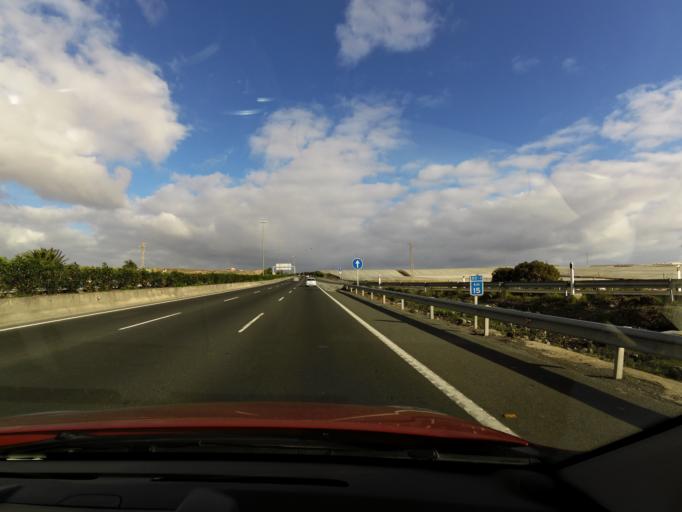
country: ES
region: Canary Islands
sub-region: Provincia de Las Palmas
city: Telde
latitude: 27.9514
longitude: -15.3872
